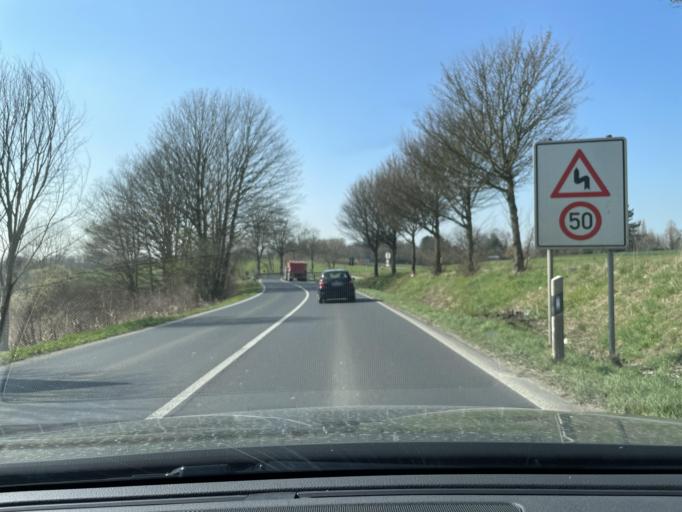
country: DE
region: North Rhine-Westphalia
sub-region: Regierungsbezirk Dusseldorf
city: Mettmann
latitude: 51.2558
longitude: 6.9447
